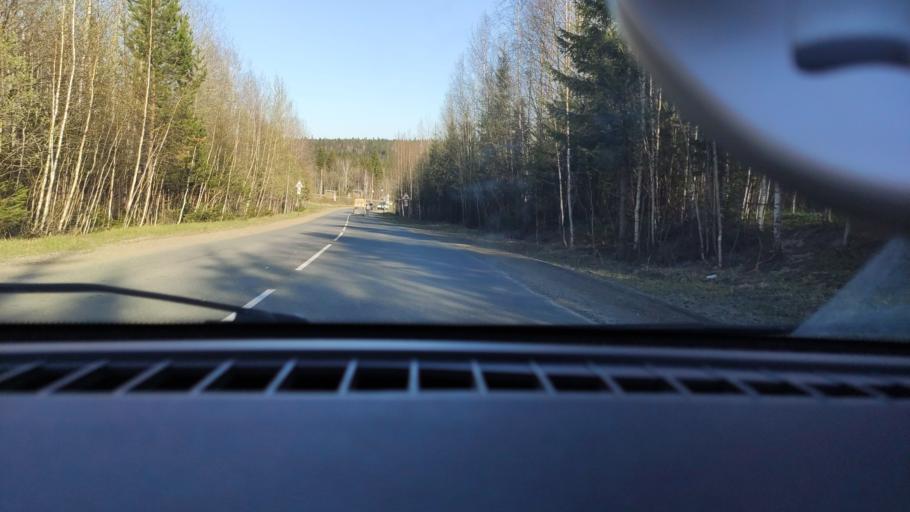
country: RU
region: Perm
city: Polazna
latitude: 58.1225
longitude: 56.4451
